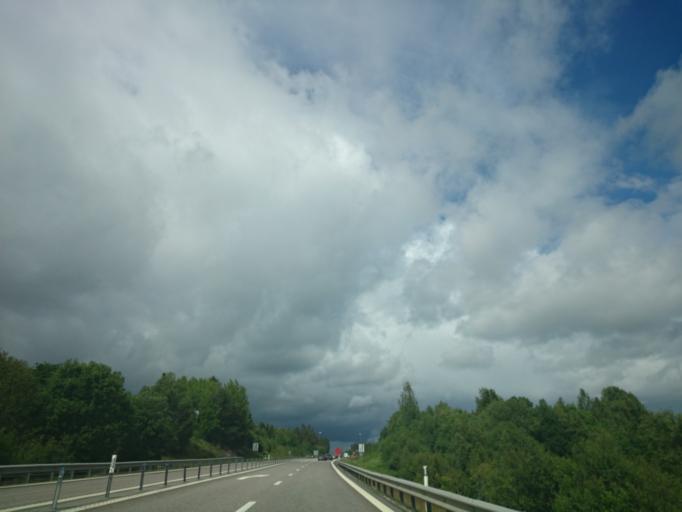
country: SE
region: Vaesternorrland
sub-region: Sundsvalls Kommun
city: Njurundabommen
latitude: 62.2274
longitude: 17.3722
